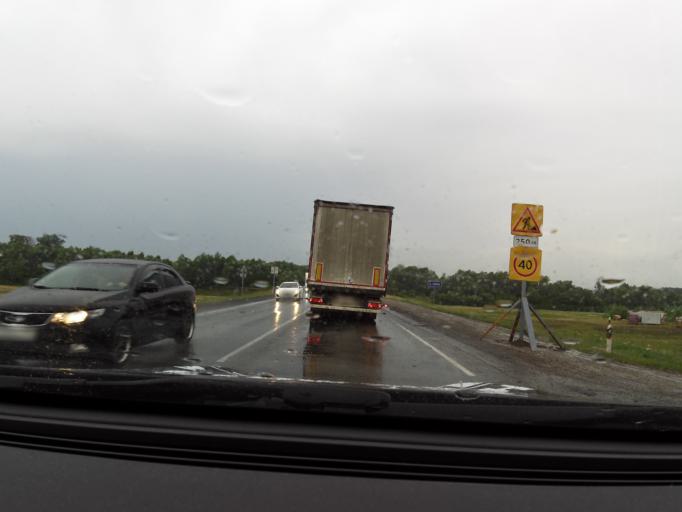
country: RU
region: Tatarstan
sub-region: Aktanyshskiy Rayon
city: Aktanysh
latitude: 55.4825
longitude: 53.8922
